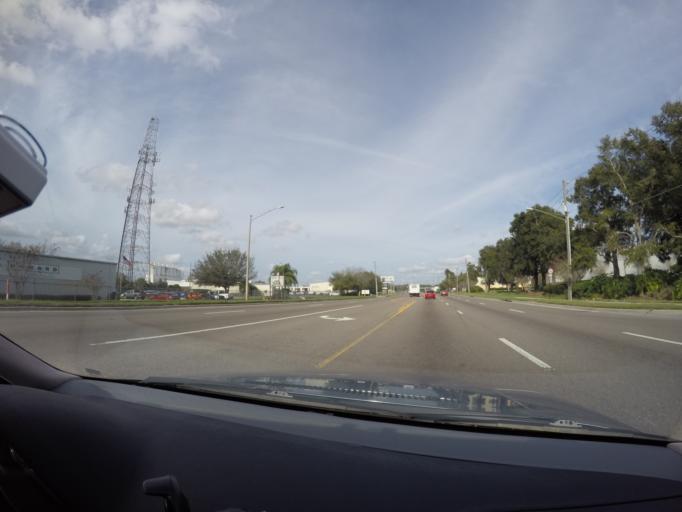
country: US
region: Florida
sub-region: Orange County
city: Belle Isle
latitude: 28.4471
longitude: -81.3645
